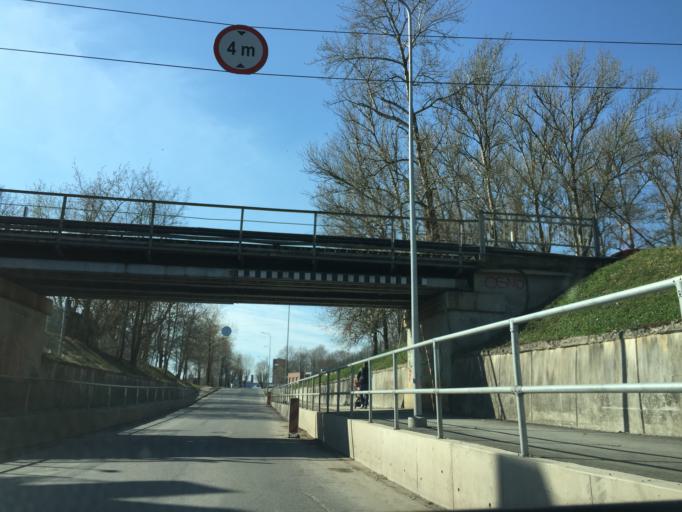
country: RU
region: Leningrad
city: Ivangorod
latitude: 59.3676
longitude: 28.2043
